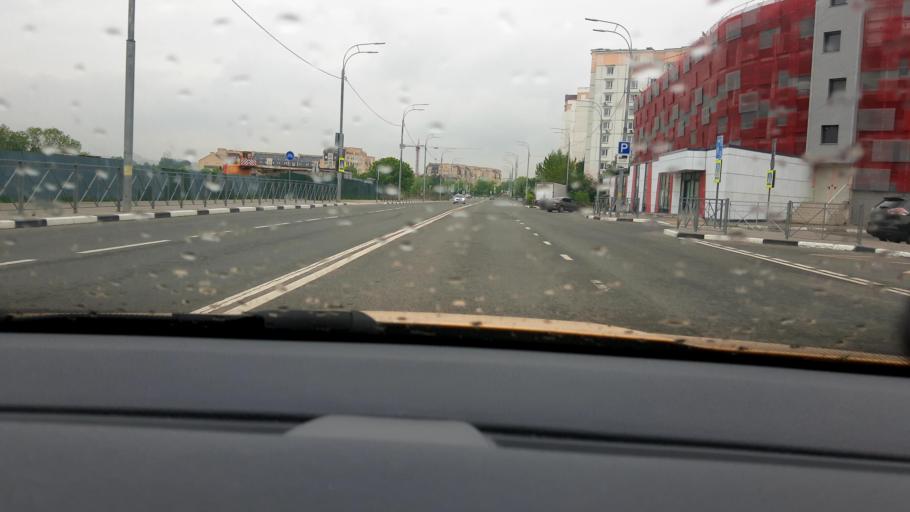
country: RU
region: Moscow
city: Yaroslavskiy
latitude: 55.9012
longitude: 37.7087
